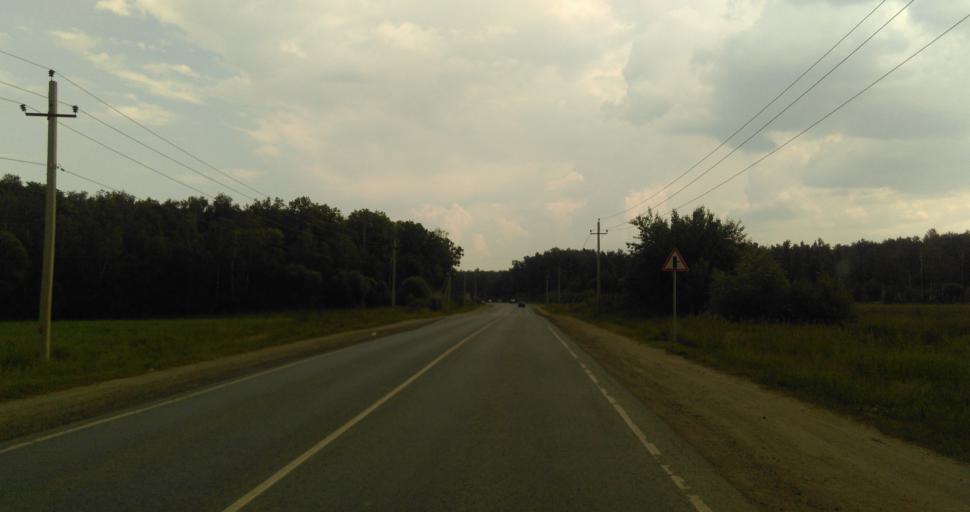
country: RU
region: Moskovskaya
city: Vostryakovo
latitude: 55.3916
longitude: 37.8592
